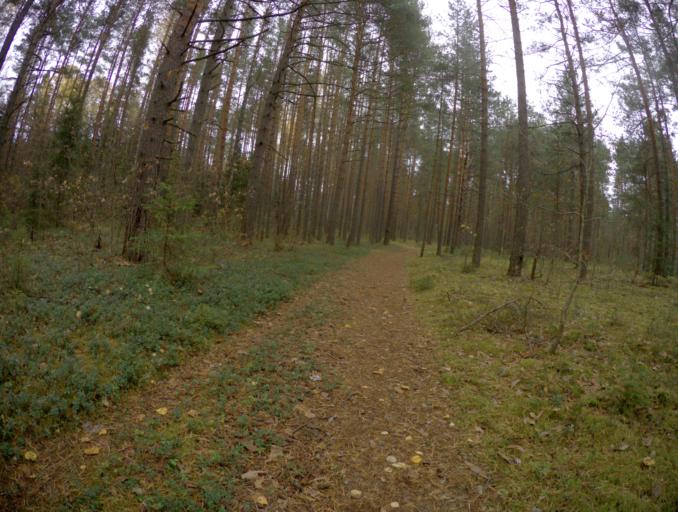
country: RU
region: Vladimir
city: Kommunar
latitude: 56.0990
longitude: 40.4683
